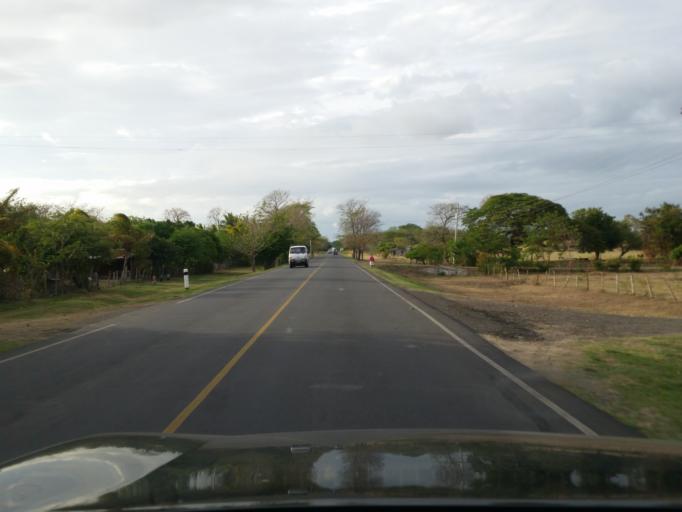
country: NI
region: Rivas
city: Belen
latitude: 11.5472
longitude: -85.8979
